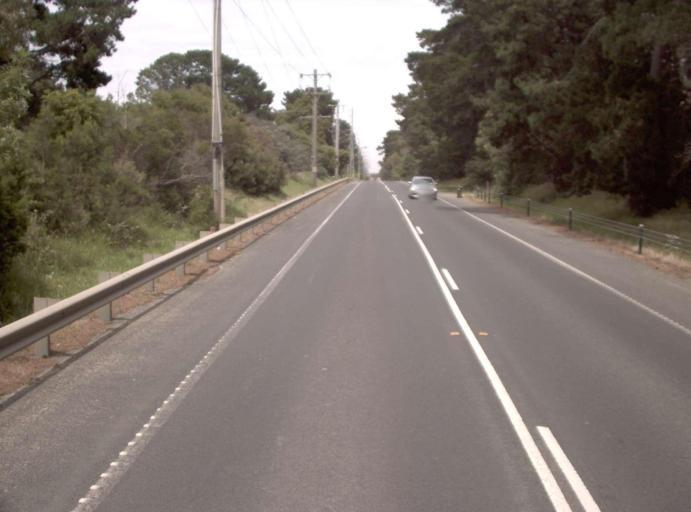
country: AU
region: Victoria
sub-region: Mornington Peninsula
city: Tyabb
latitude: -38.2625
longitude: 145.2026
